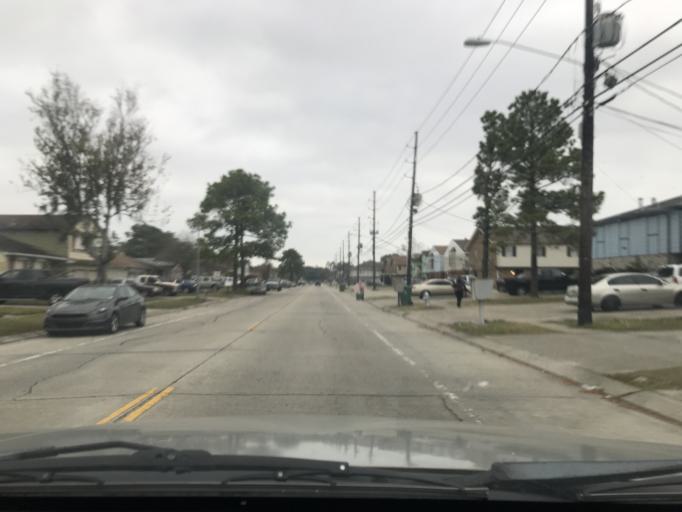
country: US
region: Louisiana
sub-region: Jefferson Parish
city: Woodmere
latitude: 29.8651
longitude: -90.0763
